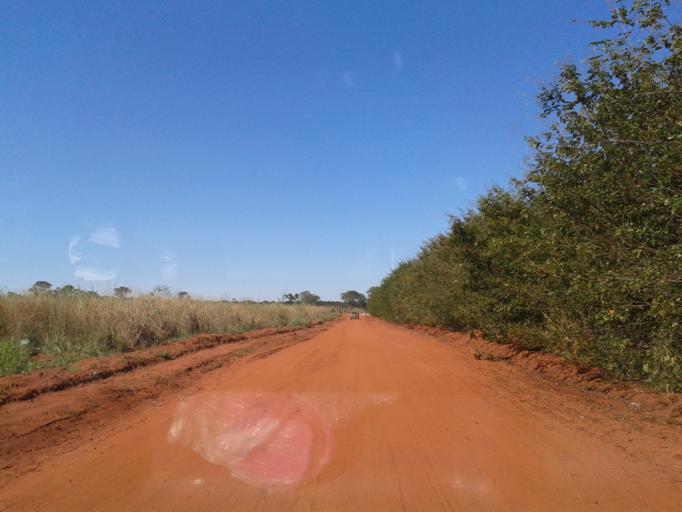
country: BR
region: Minas Gerais
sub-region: Santa Vitoria
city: Santa Vitoria
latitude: -19.0263
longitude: -50.3644
